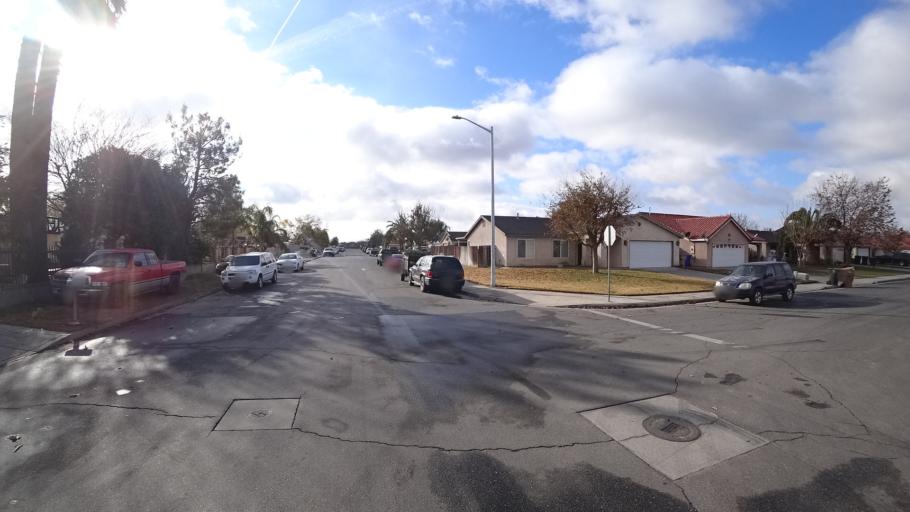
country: US
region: California
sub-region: Kern County
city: Greenfield
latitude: 35.2946
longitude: -119.0098
